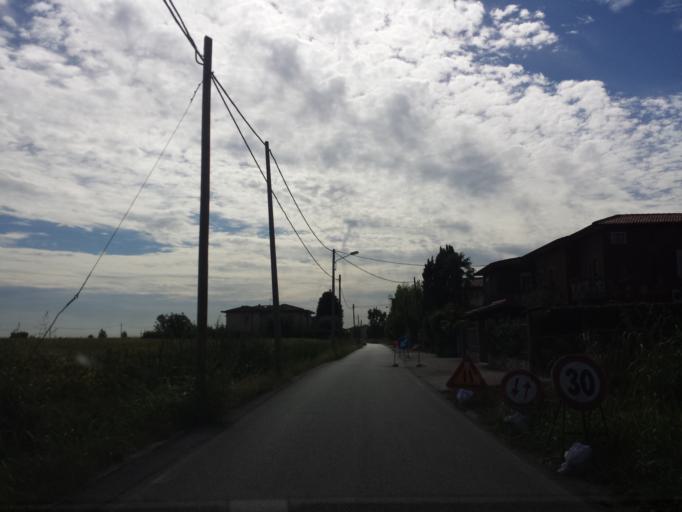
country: IT
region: Veneto
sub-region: Provincia di Vicenza
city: Vicenza
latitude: 45.5645
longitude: 11.5696
